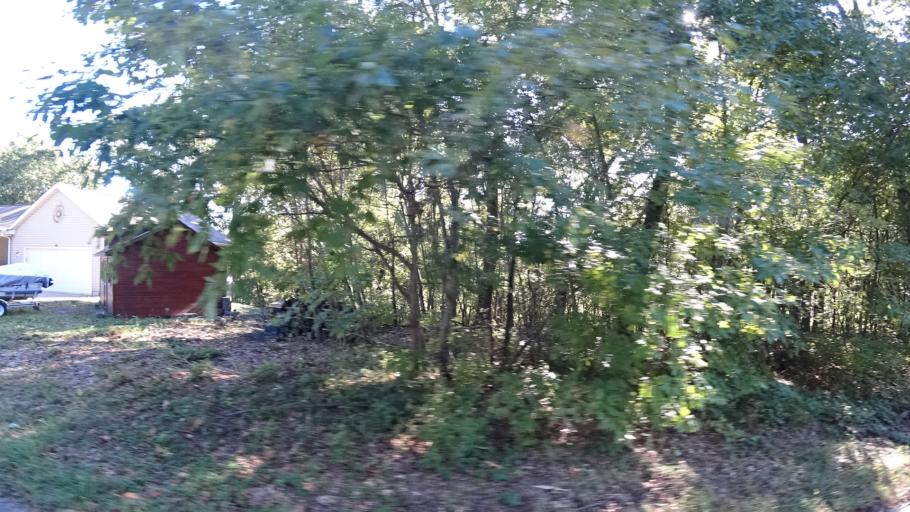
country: US
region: Indiana
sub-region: LaPorte County
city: Michigan City
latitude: 41.6935
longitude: -86.9285
